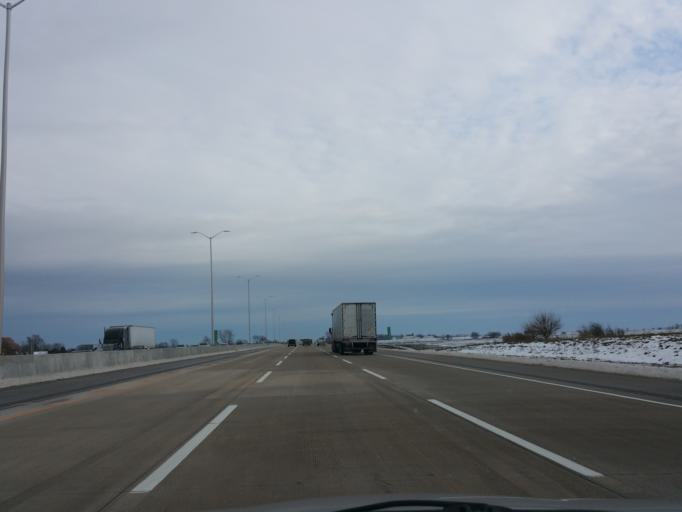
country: US
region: Illinois
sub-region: McHenry County
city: Marengo
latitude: 42.1942
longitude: -88.6658
